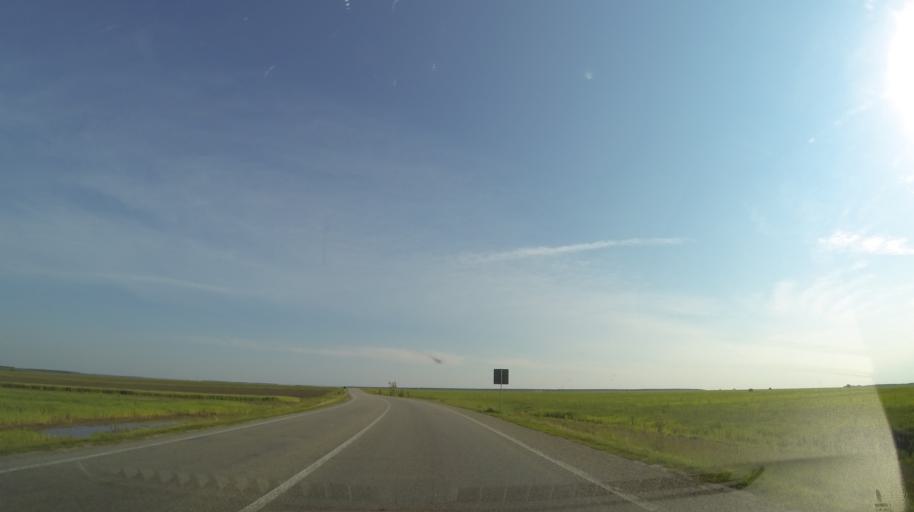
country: RO
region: Olt
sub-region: Comuna Scornicesti
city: Negreni
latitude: 44.5760
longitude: 24.6061
